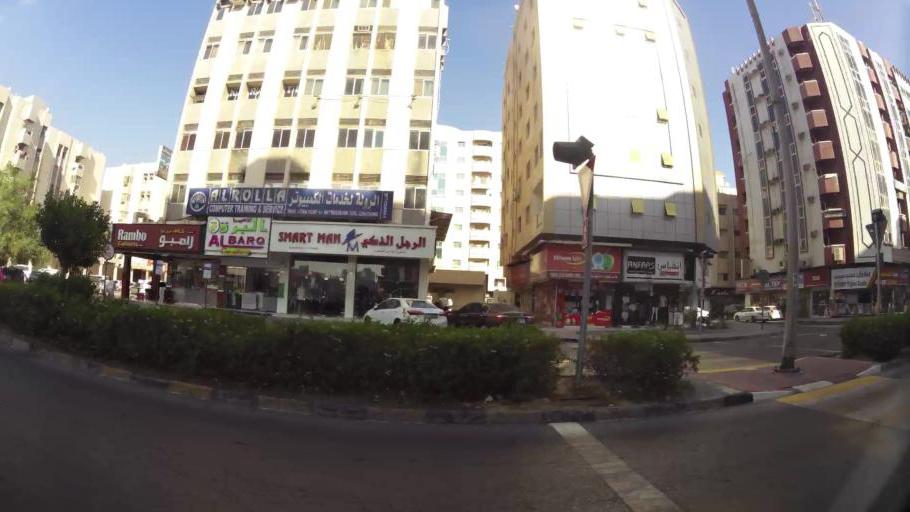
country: AE
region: Ajman
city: Ajman
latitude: 25.4108
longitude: 55.4438
